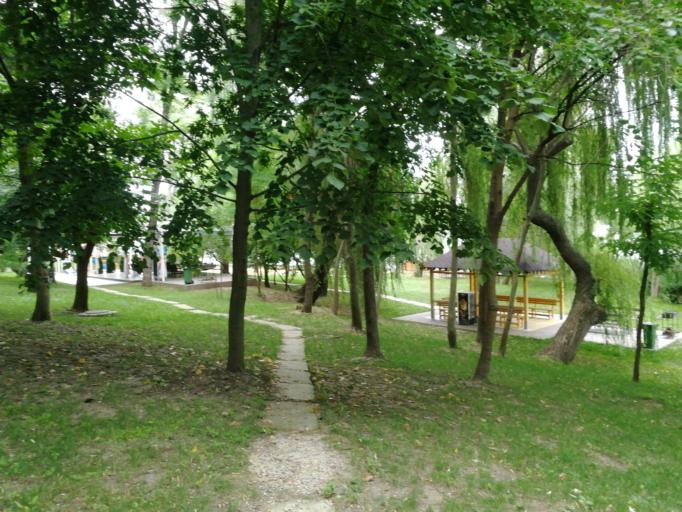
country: MD
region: Chisinau
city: Vatra
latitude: 47.1005
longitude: 28.7051
